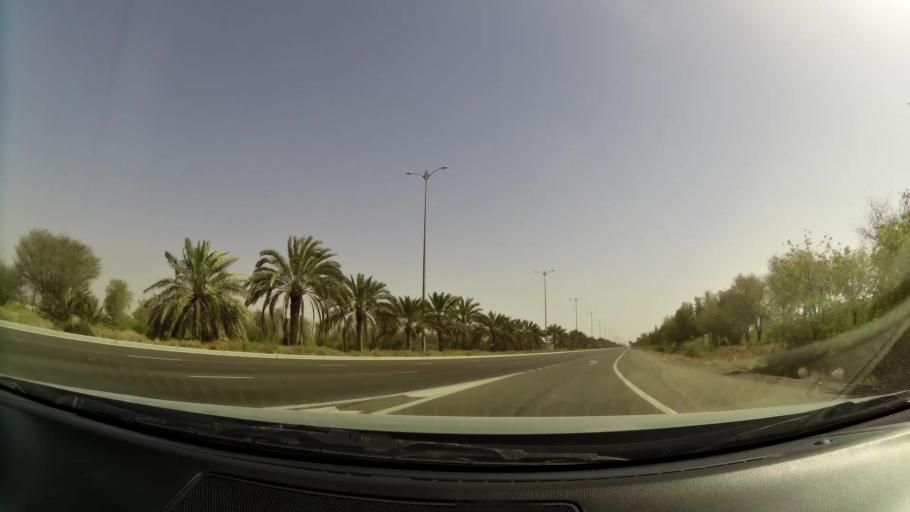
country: OM
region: Al Buraimi
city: Al Buraymi
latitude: 24.3069
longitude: 55.7938
